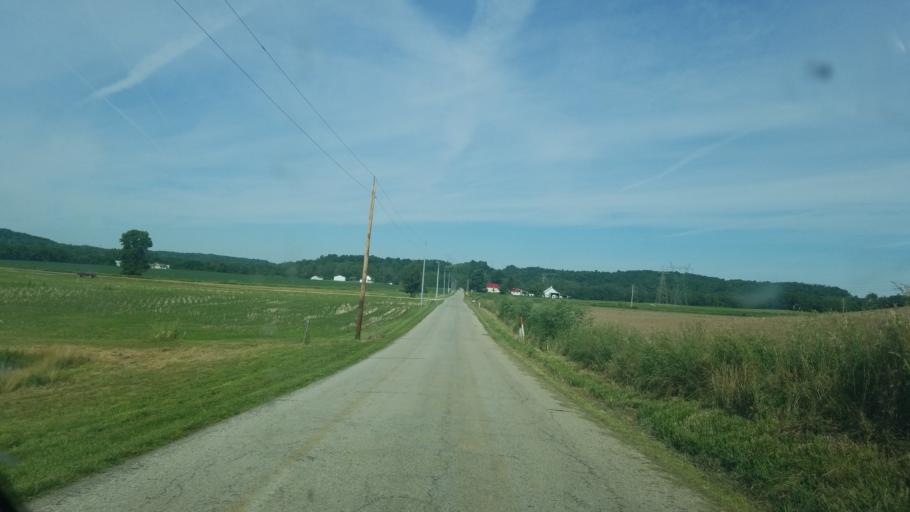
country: US
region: Ohio
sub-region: Licking County
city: Utica
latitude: 40.2084
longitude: -82.4263
